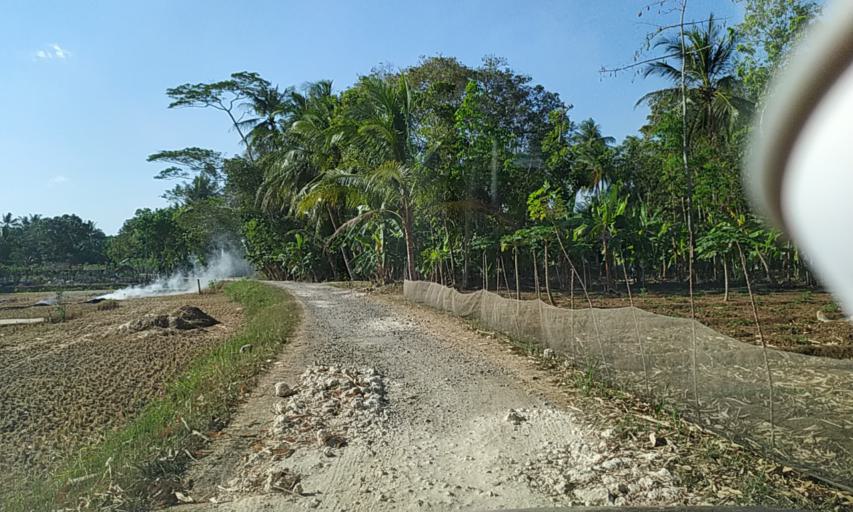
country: ID
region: West Java
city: Maruyungsari
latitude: -7.5211
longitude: 108.7419
